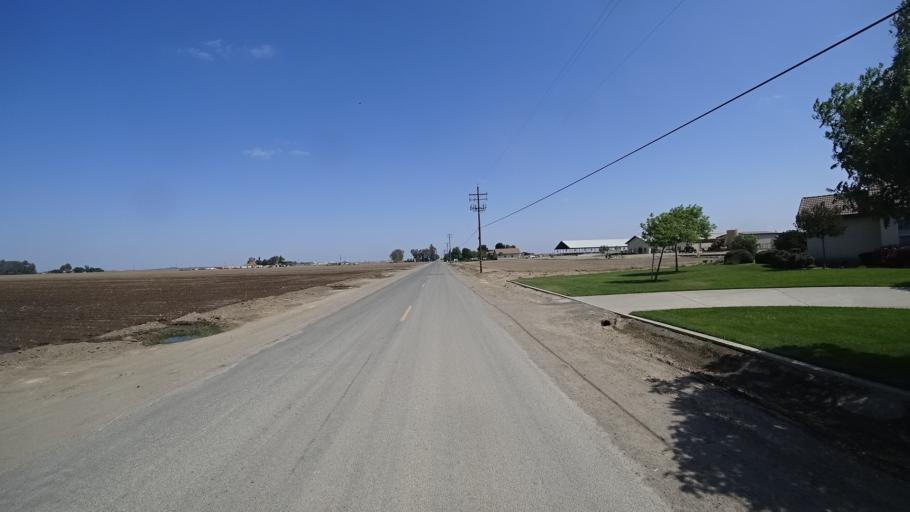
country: US
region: California
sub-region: Kings County
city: Home Garden
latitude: 36.2203
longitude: -119.6278
